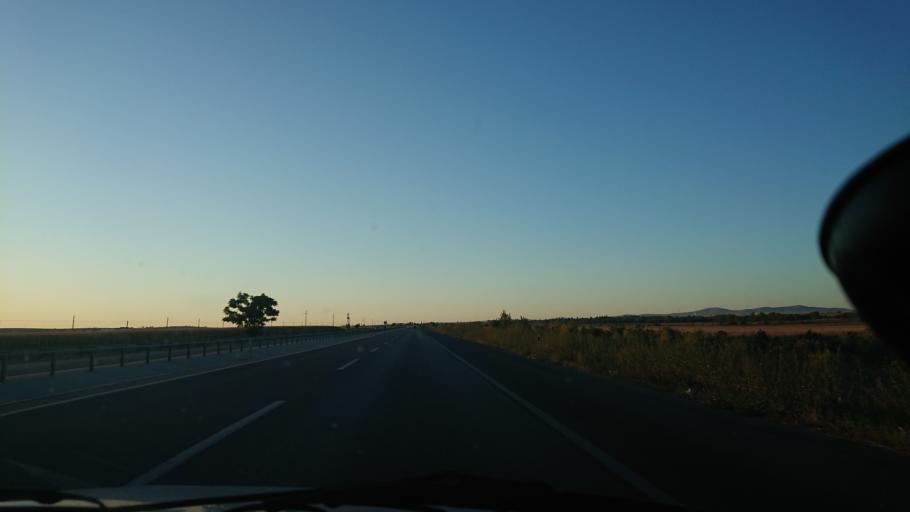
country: TR
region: Eskisehir
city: Mahmudiye
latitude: 39.5479
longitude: 30.9301
